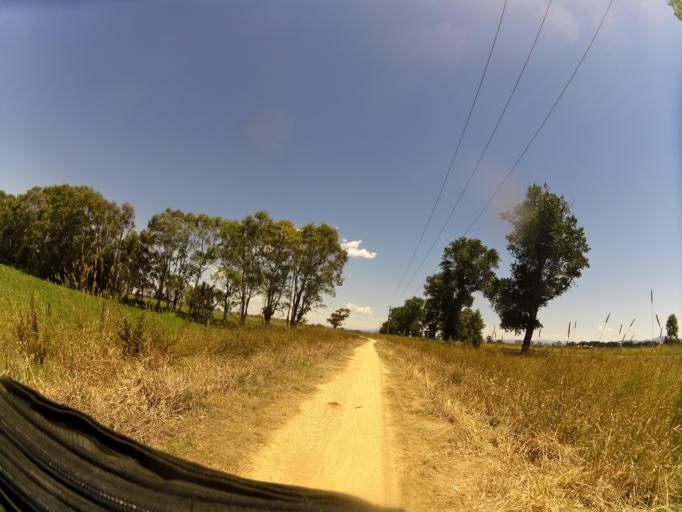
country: AU
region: Victoria
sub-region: Wellington
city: Heyfield
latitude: -37.9684
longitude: 146.9402
